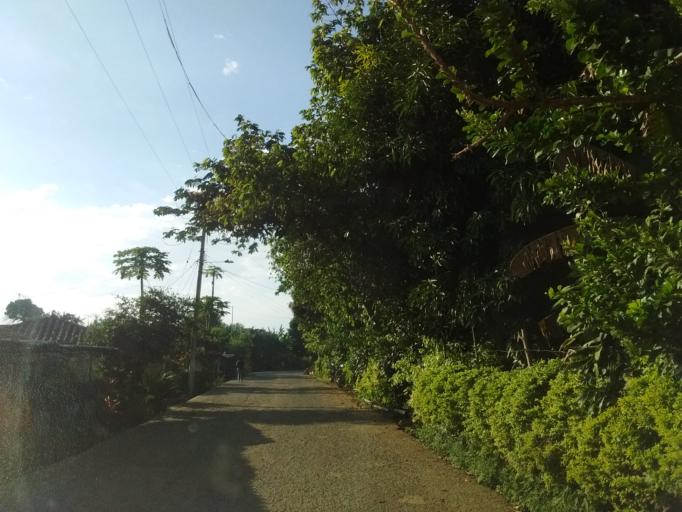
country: CO
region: Cauca
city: Puerto Tejada
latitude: 3.2149
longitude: -76.4450
